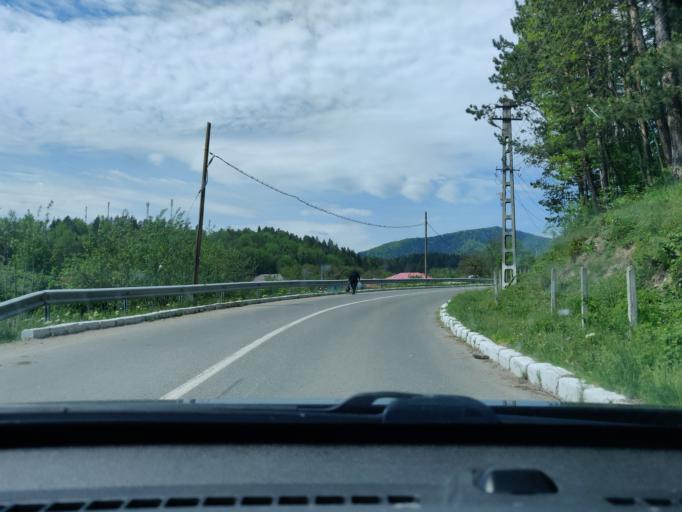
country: RO
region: Vrancea
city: Dragosloveni
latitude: 46.0001
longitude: 26.6669
